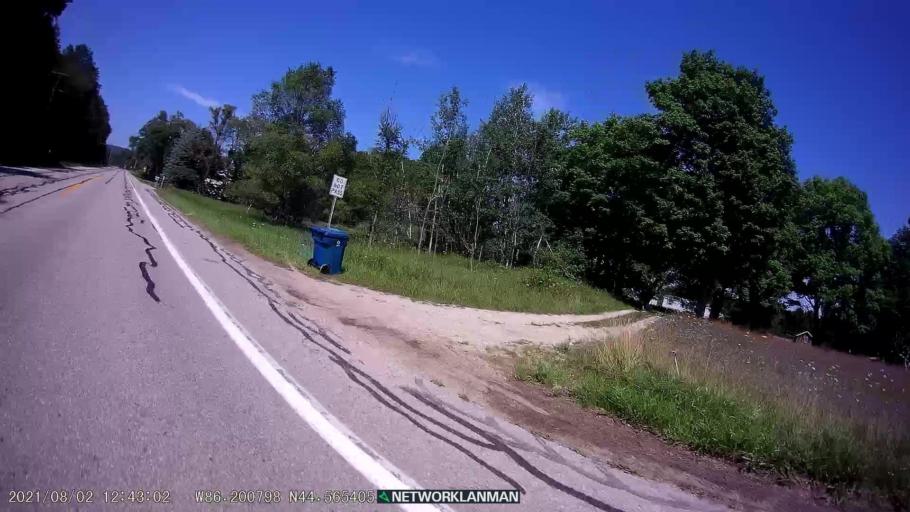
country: US
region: Michigan
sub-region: Benzie County
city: Frankfort
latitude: 44.5658
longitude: -86.2009
